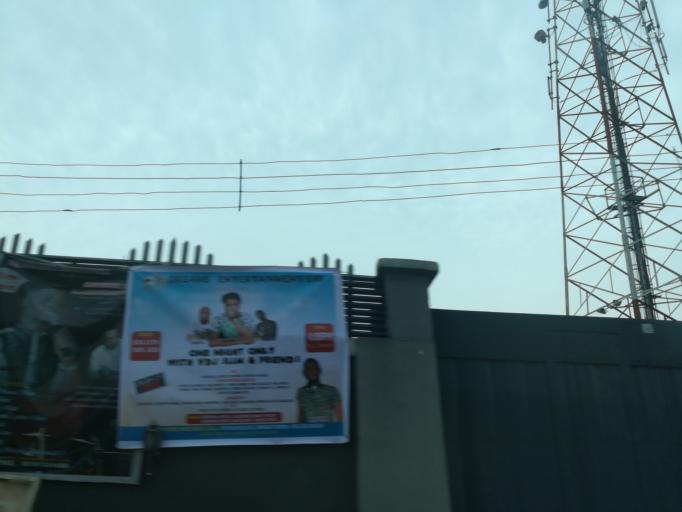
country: NG
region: Rivers
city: Port Harcourt
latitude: 4.8164
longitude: 7.0246
